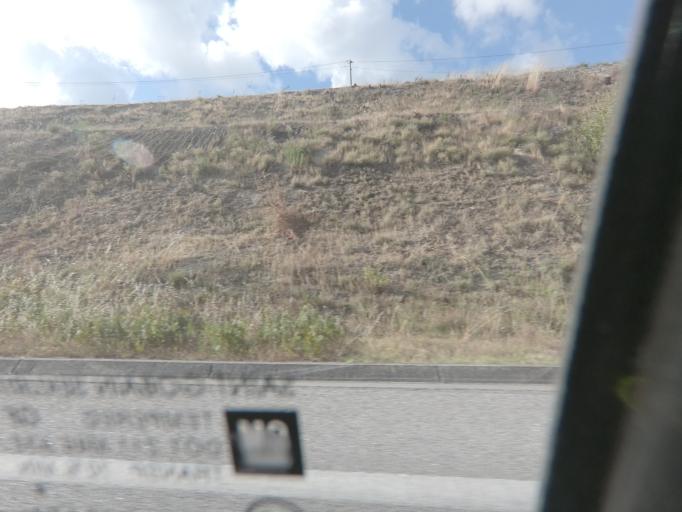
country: PT
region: Porto
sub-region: Amarante
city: Figueiro
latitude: 41.2371
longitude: -8.1914
